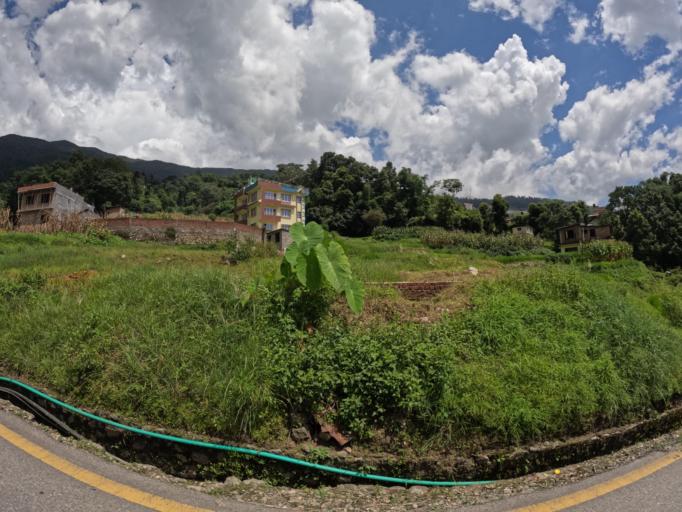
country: NP
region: Central Region
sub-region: Bagmati Zone
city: Kathmandu
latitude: 27.7985
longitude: 85.3298
